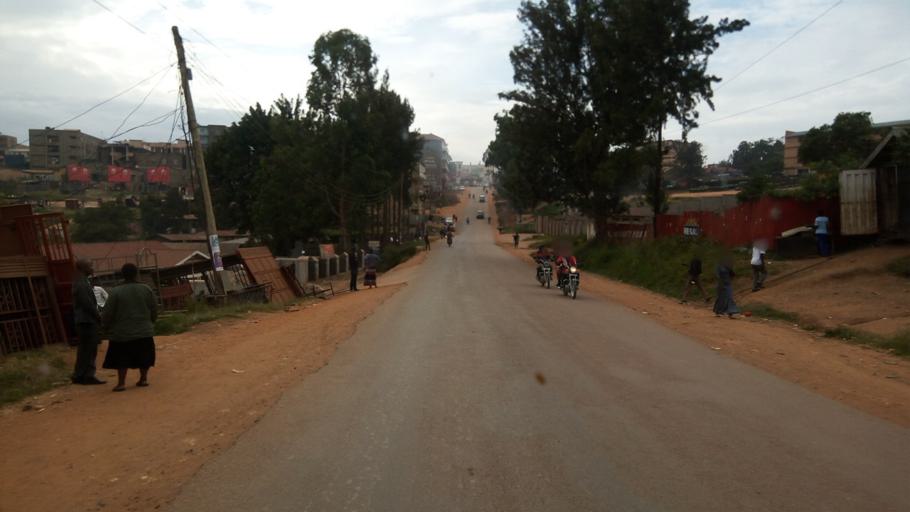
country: UG
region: Western Region
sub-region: Mbarara District
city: Mbarara
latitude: -0.6056
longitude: 30.6582
